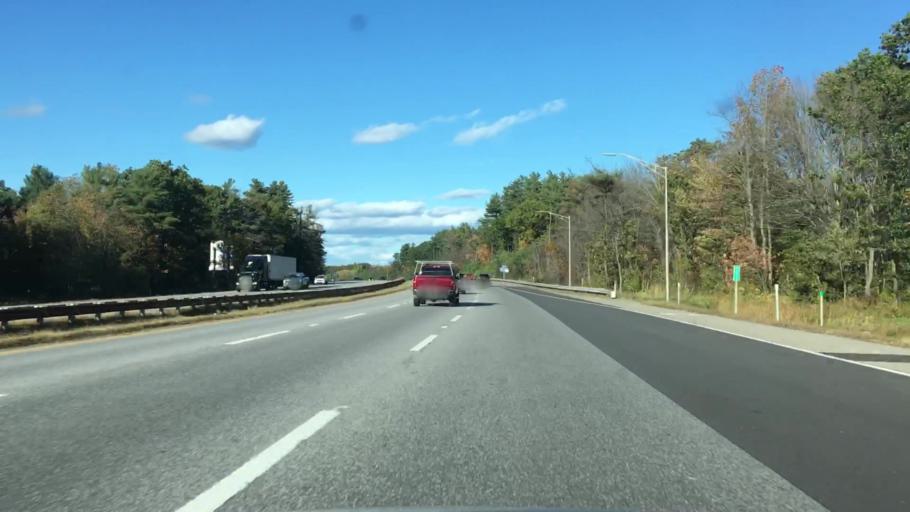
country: US
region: Maine
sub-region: York County
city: Biddeford
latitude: 43.4845
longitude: -70.4957
